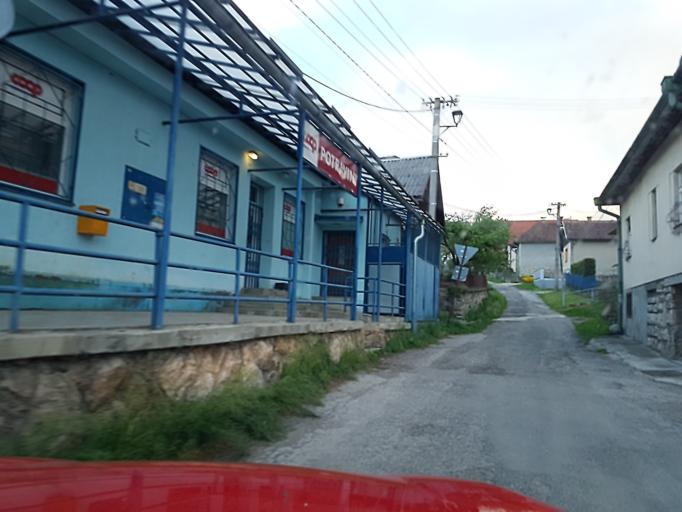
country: SK
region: Zilinsky
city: Ruzomberok
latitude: 49.1251
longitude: 19.4153
